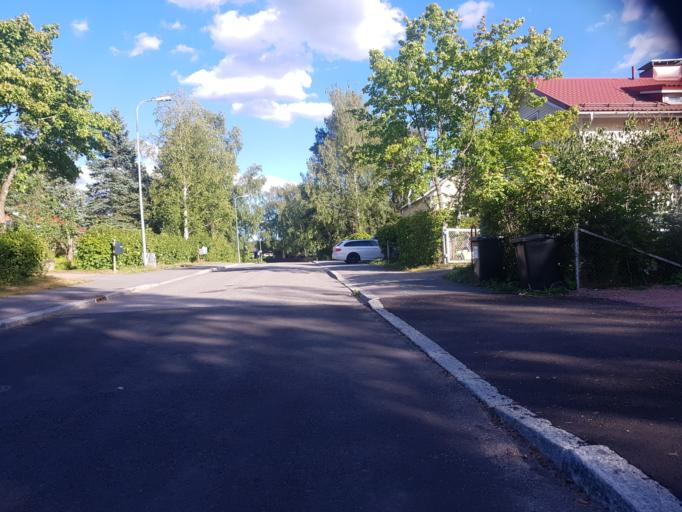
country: FI
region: Uusimaa
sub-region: Helsinki
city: Vantaa
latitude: 60.2846
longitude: 25.0065
